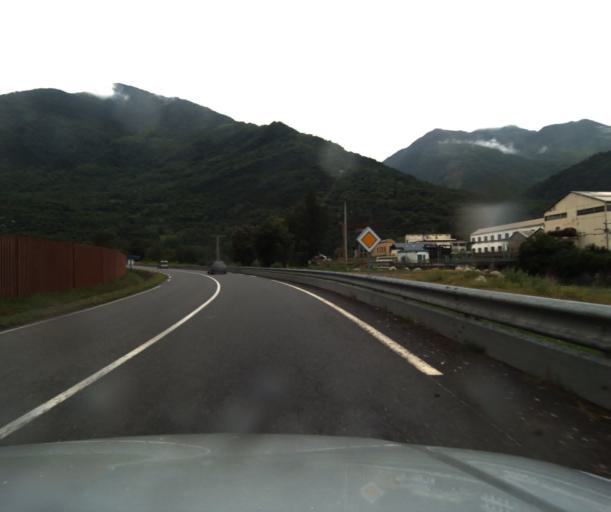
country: FR
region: Midi-Pyrenees
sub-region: Departement des Hautes-Pyrenees
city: Pierrefitte-Nestalas
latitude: 42.9572
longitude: -0.0655
